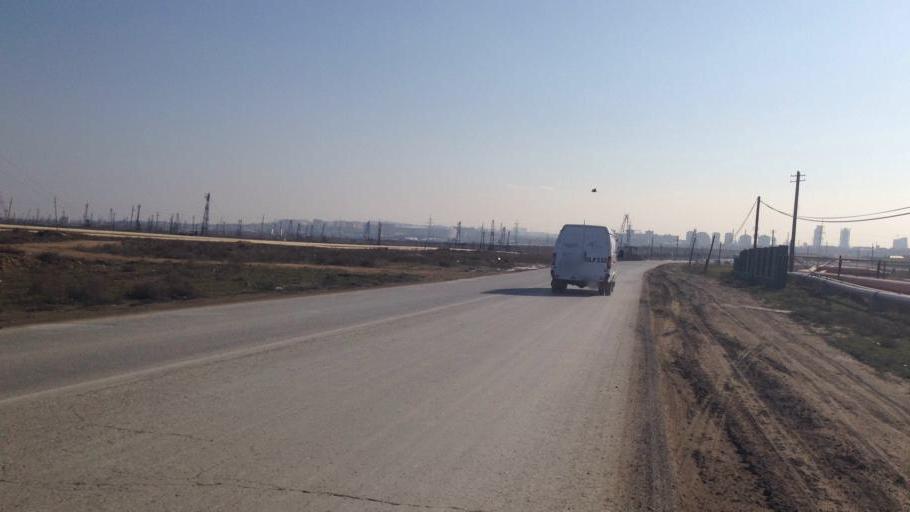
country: AZ
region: Baki
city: Balakhani
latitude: 40.4600
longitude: 49.8905
